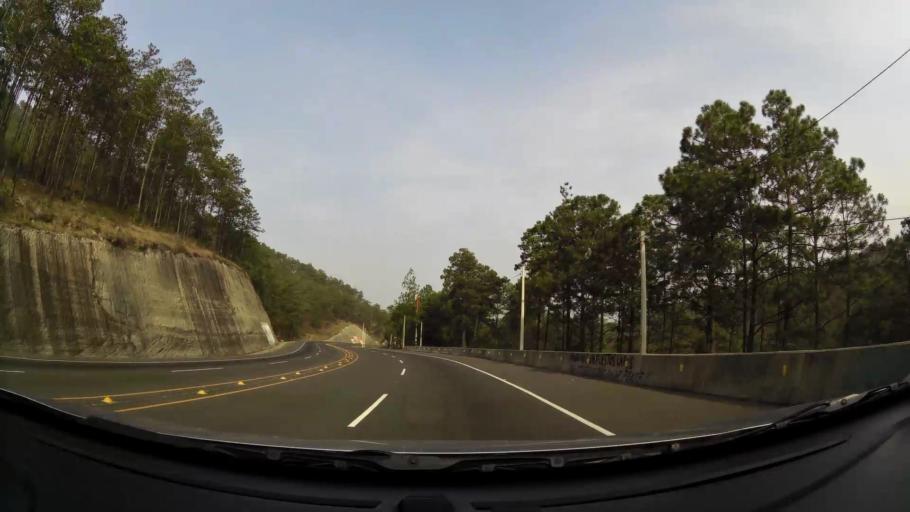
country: HN
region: Francisco Morazan
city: Zambrano
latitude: 14.2855
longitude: -87.4503
